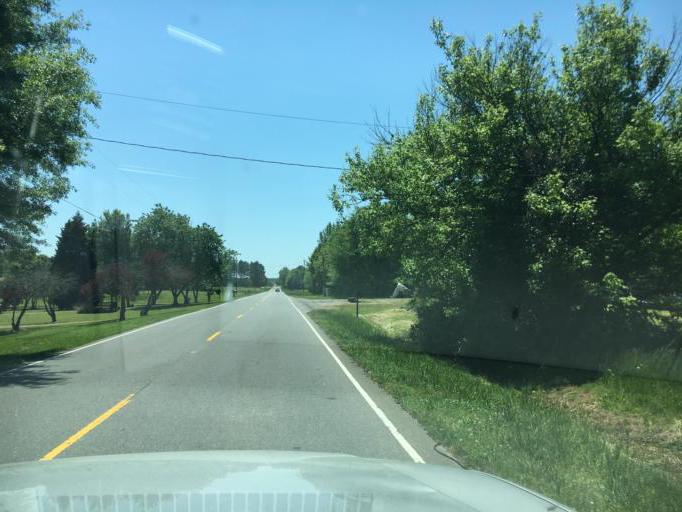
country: US
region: South Carolina
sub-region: Cherokee County
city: Blacksburg
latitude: 35.1964
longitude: -81.5646
